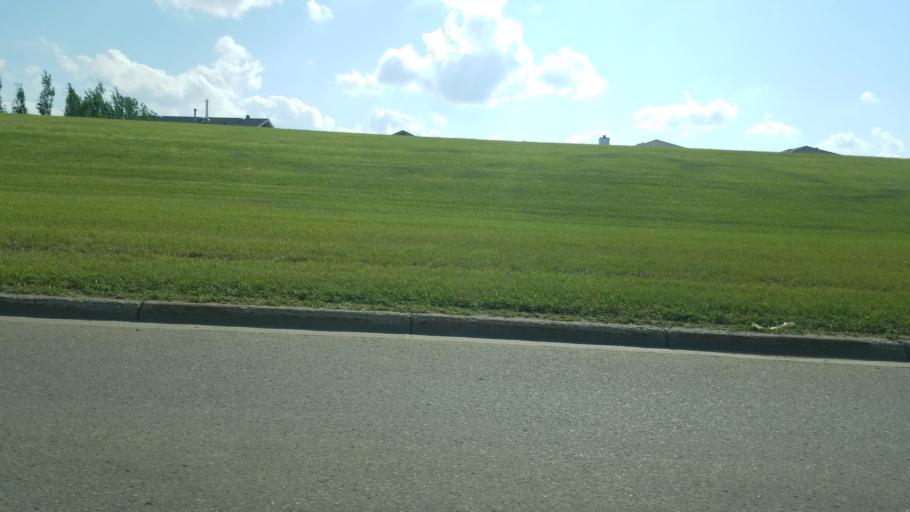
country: CA
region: Saskatchewan
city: Lloydminster
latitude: 53.2742
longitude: -110.0335
